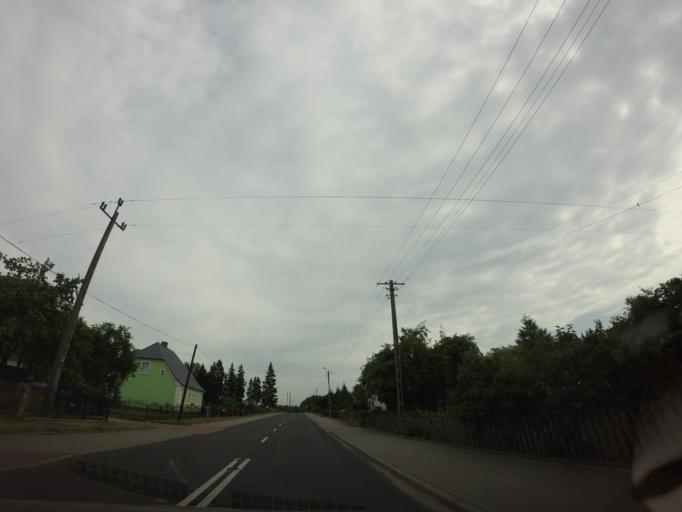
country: PL
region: West Pomeranian Voivodeship
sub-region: Powiat drawski
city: Wierzchowo
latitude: 53.4350
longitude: 16.2036
